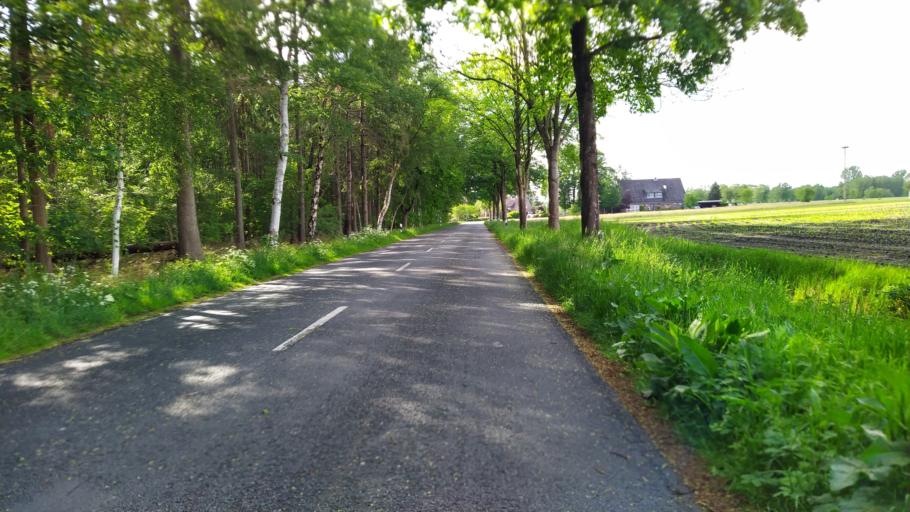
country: DE
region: Lower Saxony
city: Brest
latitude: 53.4331
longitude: 9.3557
